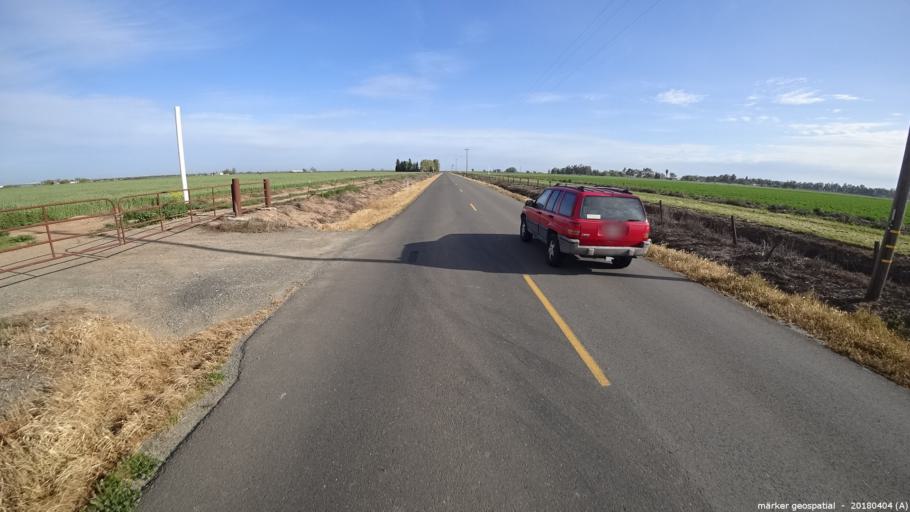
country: US
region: California
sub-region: Sacramento County
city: Herald
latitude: 38.3206
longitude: -121.3014
